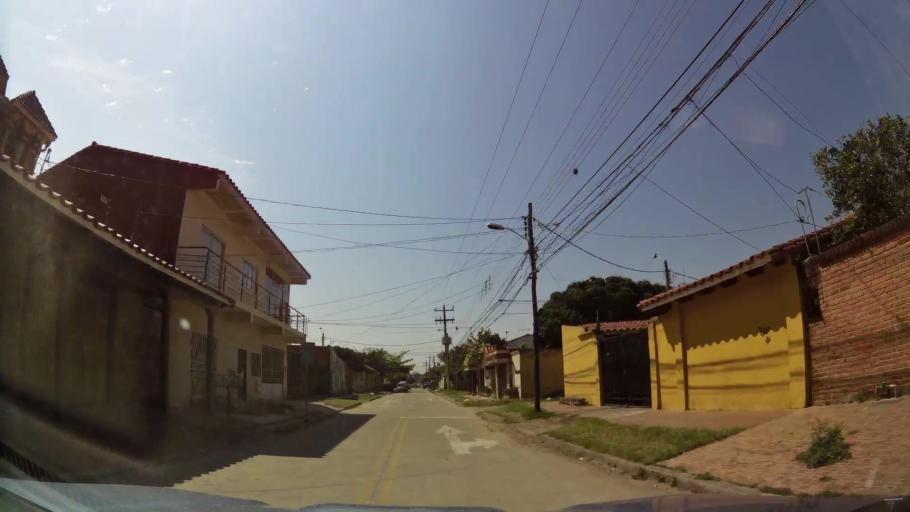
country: BO
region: Santa Cruz
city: Santa Cruz de la Sierra
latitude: -17.7490
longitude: -63.1893
